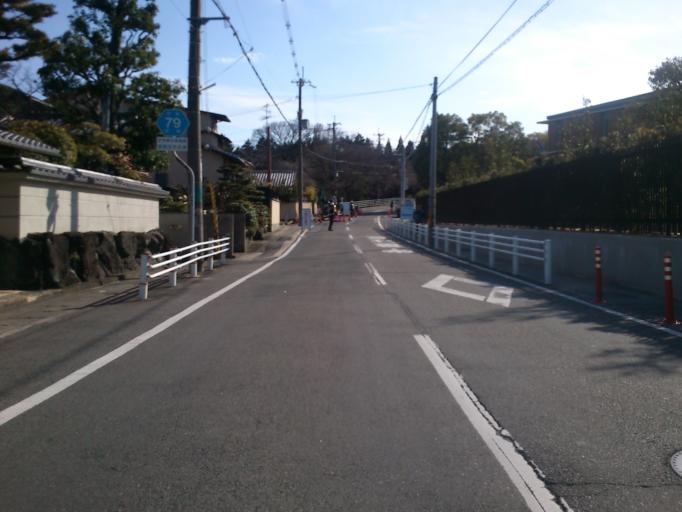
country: JP
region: Kyoto
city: Muko
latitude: 34.9251
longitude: 135.6859
